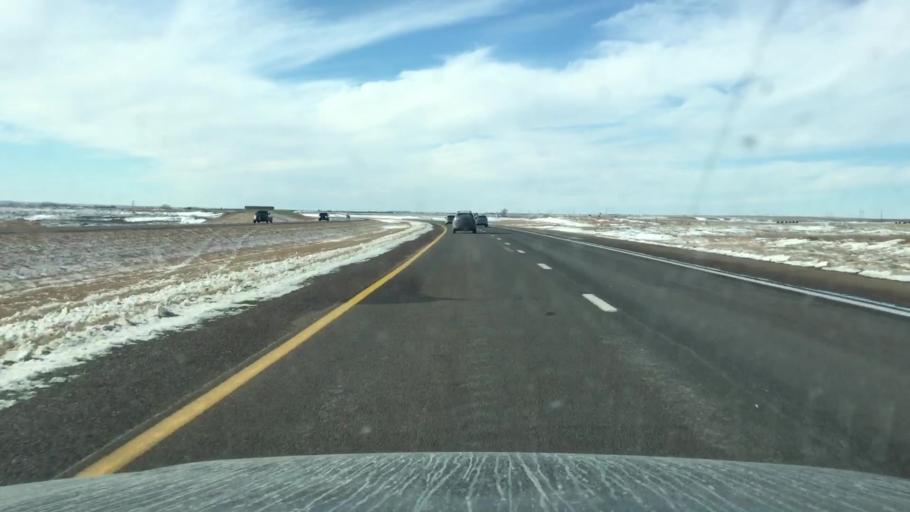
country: US
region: Kansas
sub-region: Ellis County
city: Hays
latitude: 38.9205
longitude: -99.3775
